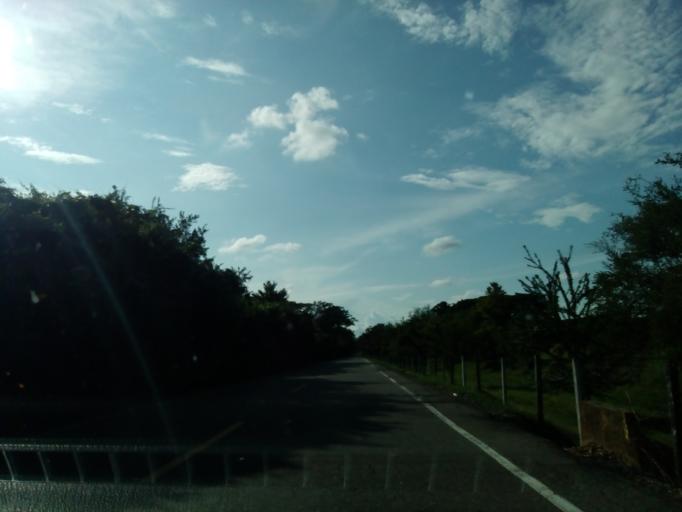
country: CO
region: Boyaca
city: Puerto Boyaca
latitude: 5.9377
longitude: -74.5527
